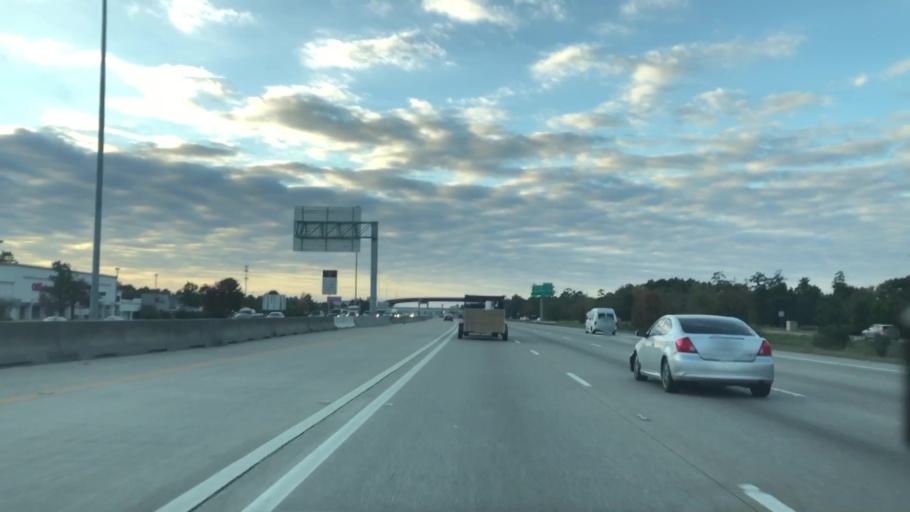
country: US
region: Texas
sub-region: Montgomery County
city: Oak Ridge North
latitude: 30.1628
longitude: -95.4492
